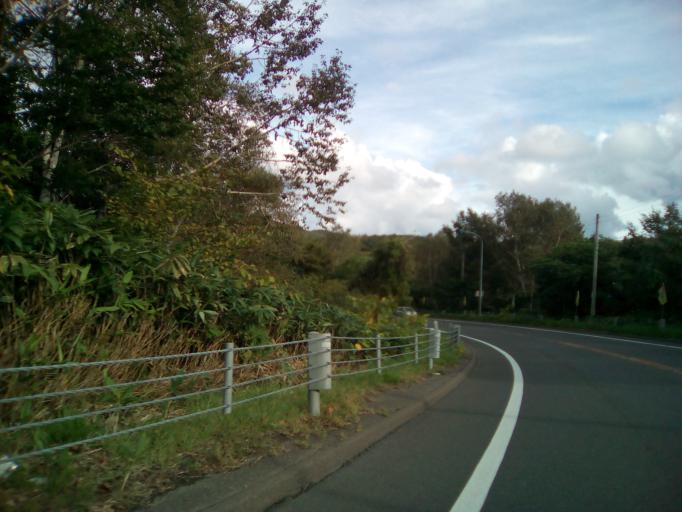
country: JP
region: Hokkaido
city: Niseko Town
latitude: 42.6854
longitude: 140.8360
